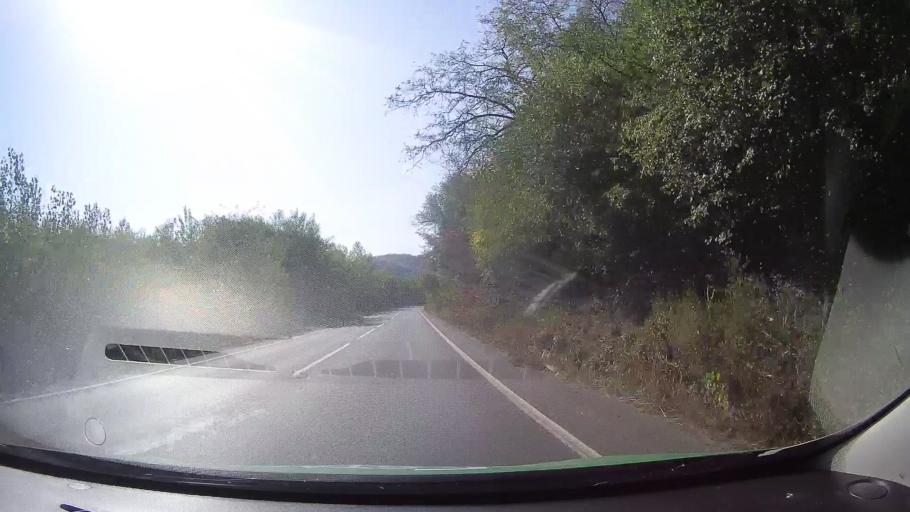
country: RO
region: Arad
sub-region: Oras Lipova
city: Lipova
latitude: 46.1051
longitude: 21.7563
